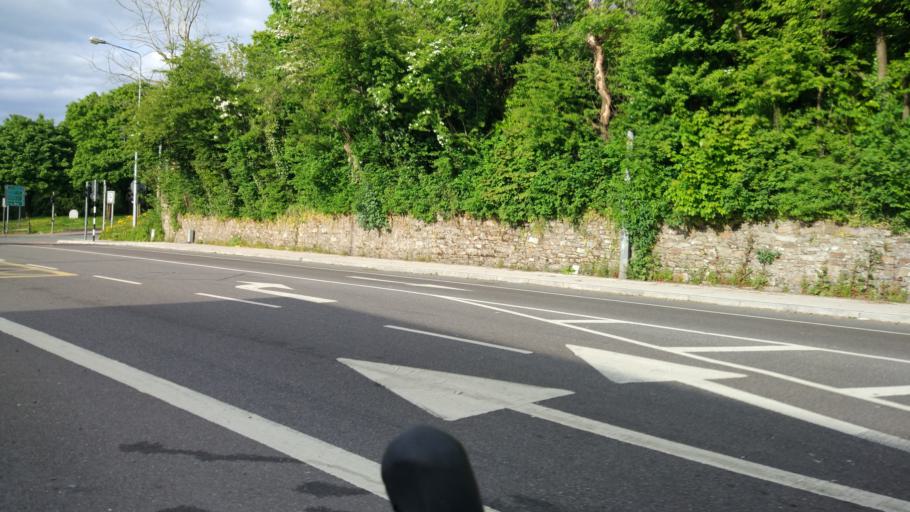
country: IE
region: Munster
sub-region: County Cork
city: Cork
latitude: 51.9143
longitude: -8.4474
